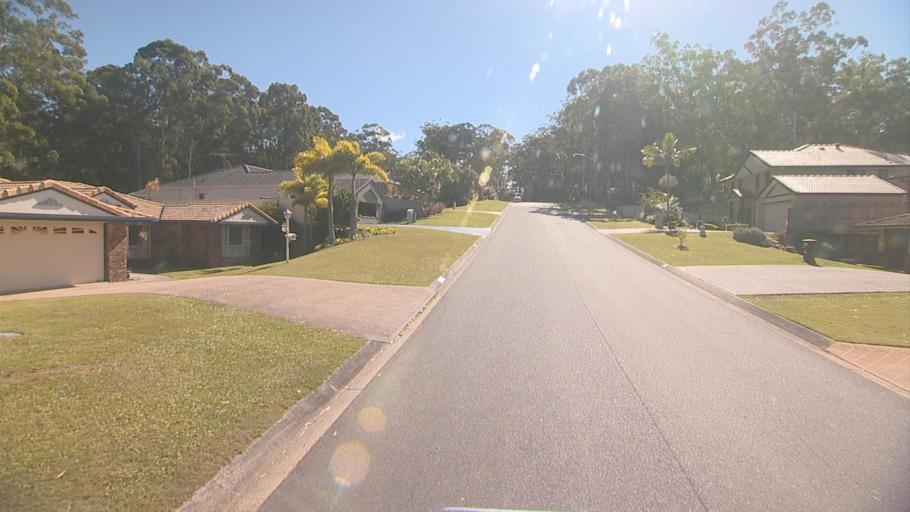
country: AU
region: Queensland
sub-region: Logan
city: Slacks Creek
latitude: -27.6413
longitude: 153.1874
